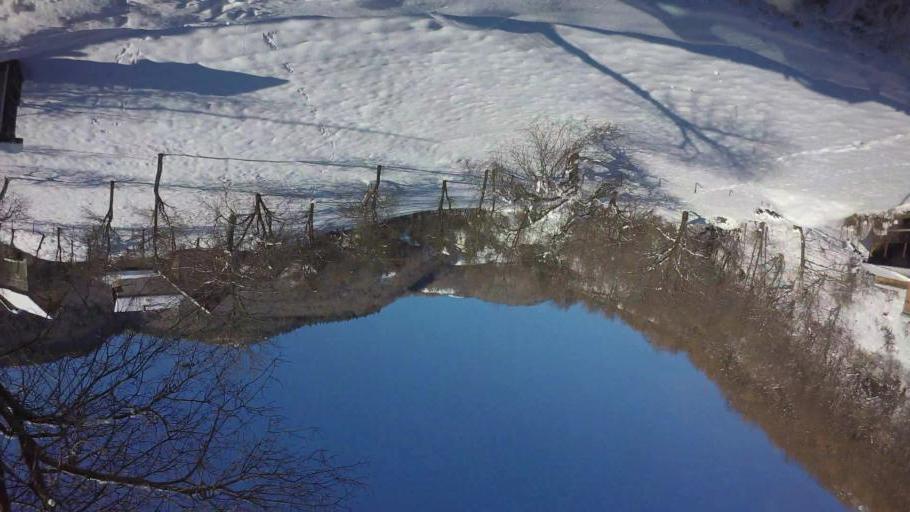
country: BA
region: Federation of Bosnia and Herzegovina
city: Kobilja Glava
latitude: 43.8979
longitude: 18.4131
